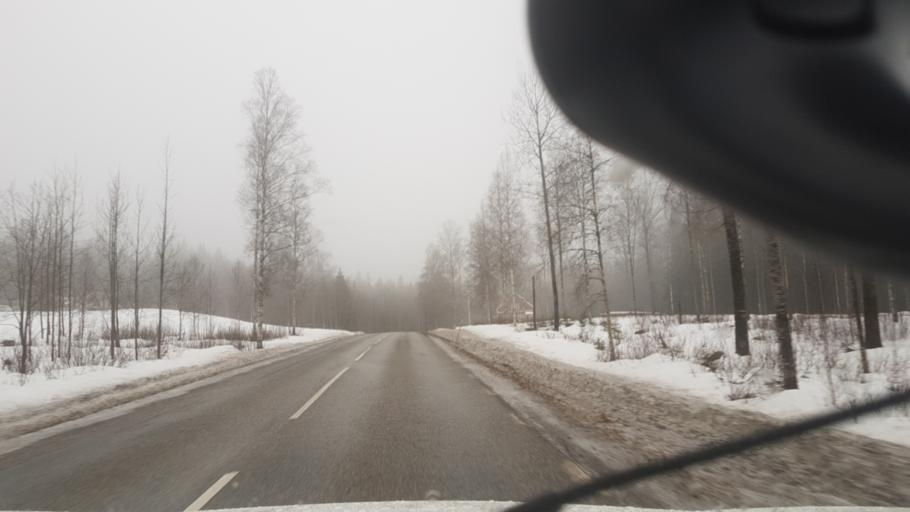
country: SE
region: Vaermland
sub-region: Eda Kommun
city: Amotfors
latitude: 59.5797
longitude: 12.2567
